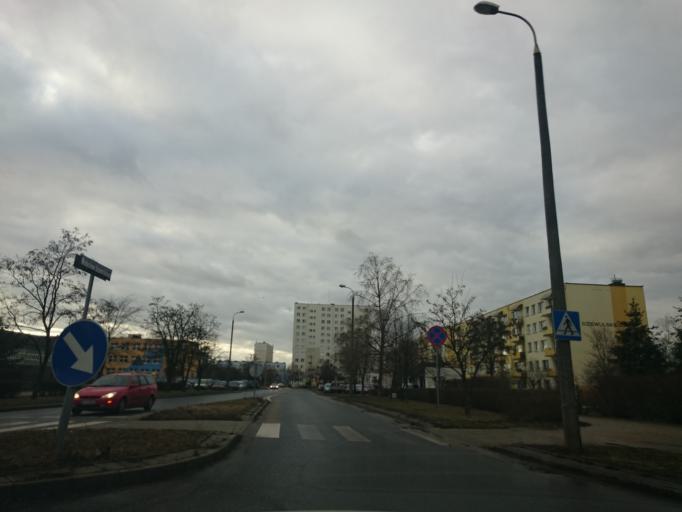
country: PL
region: Kujawsko-Pomorskie
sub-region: Powiat torunski
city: Lubicz Dolny
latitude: 53.0296
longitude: 18.6711
